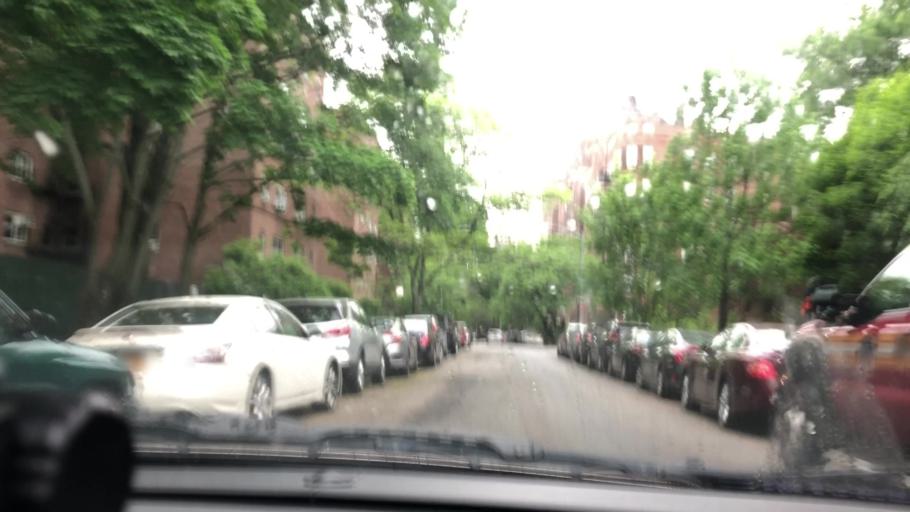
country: US
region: New York
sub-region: Queens County
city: Borough of Queens
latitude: 40.7168
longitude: -73.8380
